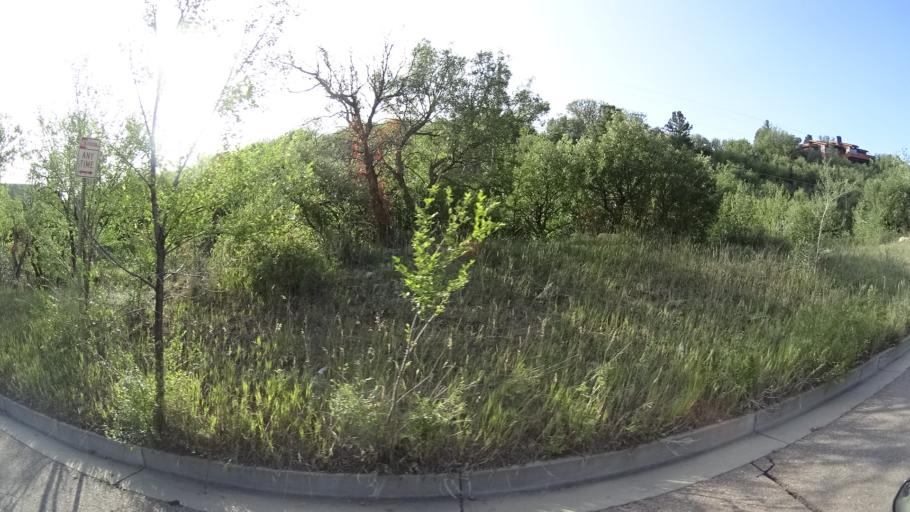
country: US
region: Colorado
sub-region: El Paso County
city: Colorado Springs
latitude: 38.8129
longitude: -104.8542
